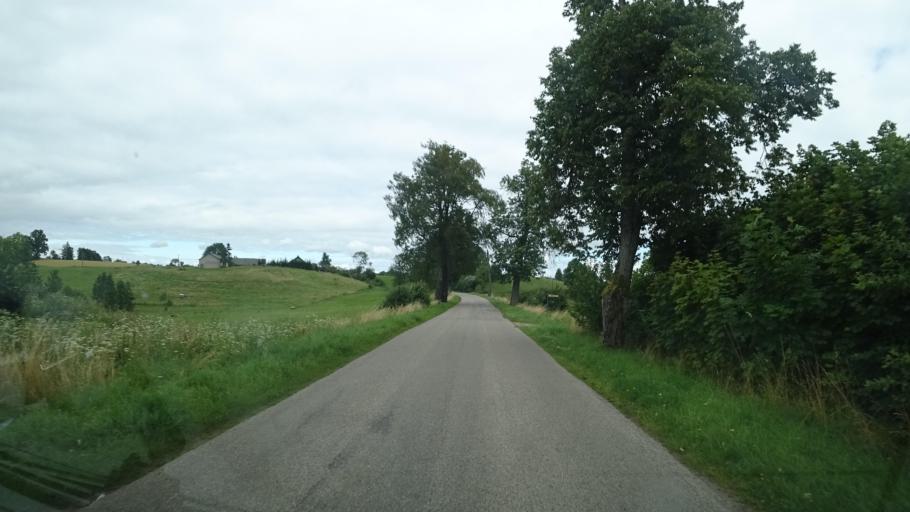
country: PL
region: Podlasie
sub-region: Powiat suwalski
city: Filipow
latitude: 54.2874
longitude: 22.5751
